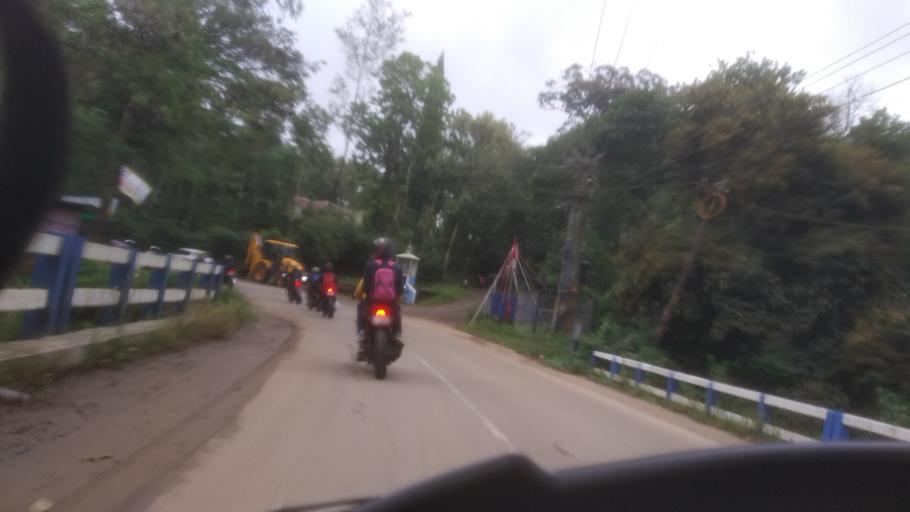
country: IN
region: Tamil Nadu
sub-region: Theni
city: Kombai
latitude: 9.8965
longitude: 77.1889
